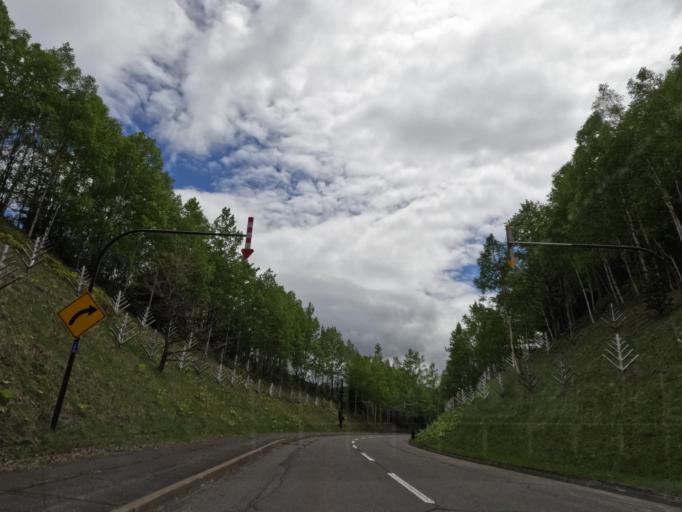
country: JP
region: Hokkaido
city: Kamikawa
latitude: 43.6674
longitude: 143.0378
